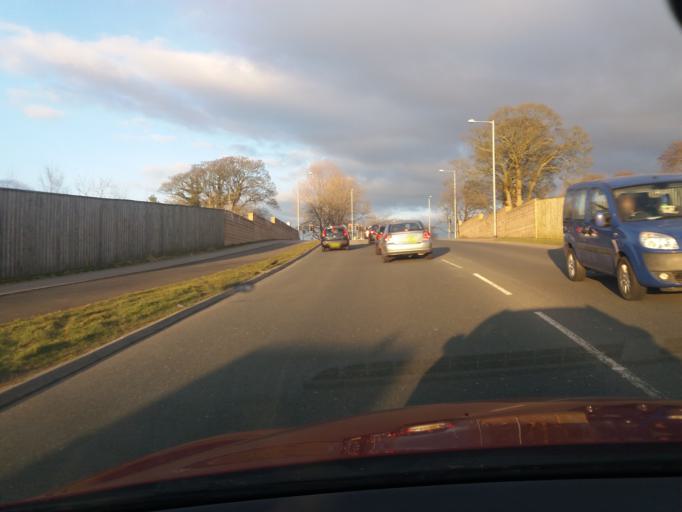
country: GB
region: England
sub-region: Lancashire
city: Chorley
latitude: 53.6730
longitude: -2.6357
